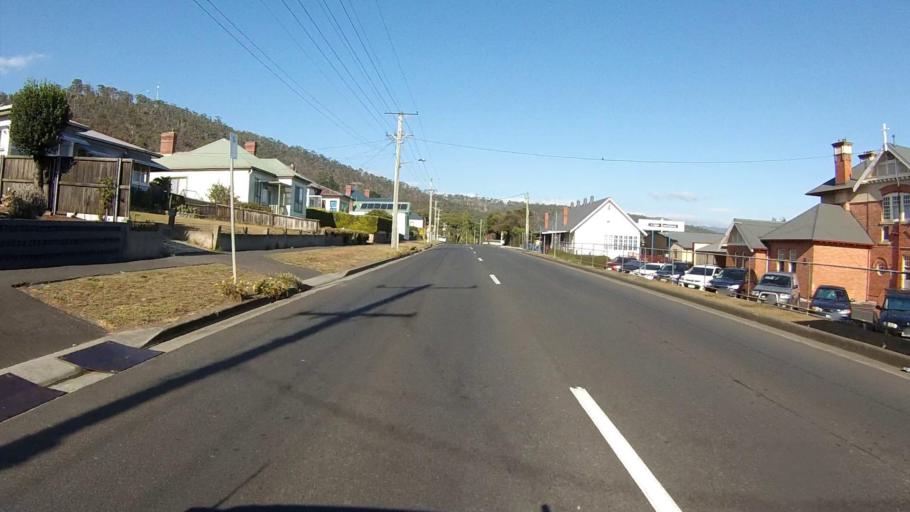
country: AU
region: Tasmania
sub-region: Derwent Valley
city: New Norfolk
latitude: -42.7806
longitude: 147.0568
